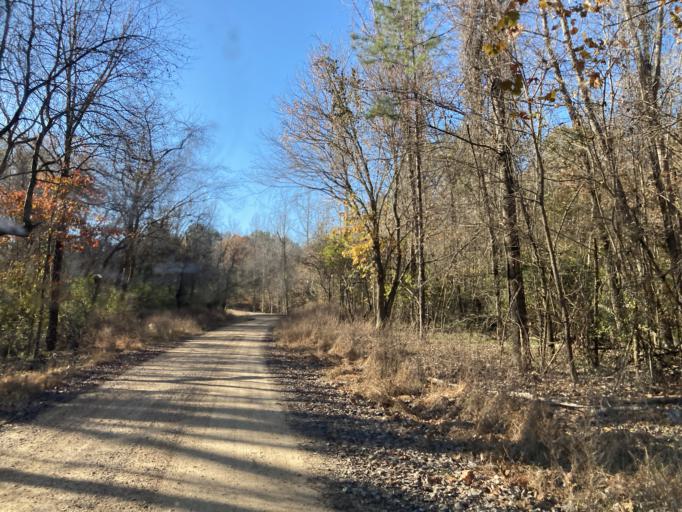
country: US
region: Mississippi
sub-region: Yazoo County
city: Yazoo City
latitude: 32.7055
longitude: -90.4711
